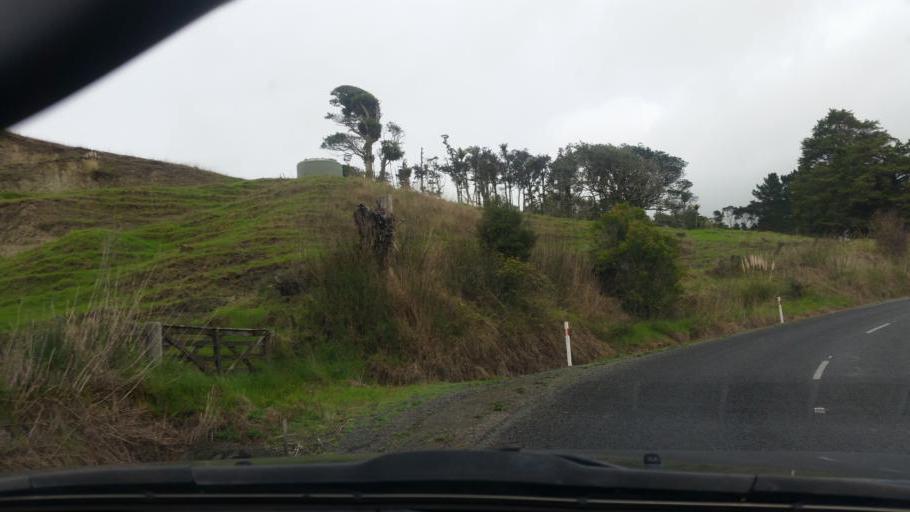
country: NZ
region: Northland
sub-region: Kaipara District
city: Dargaville
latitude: -36.0124
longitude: 173.9794
